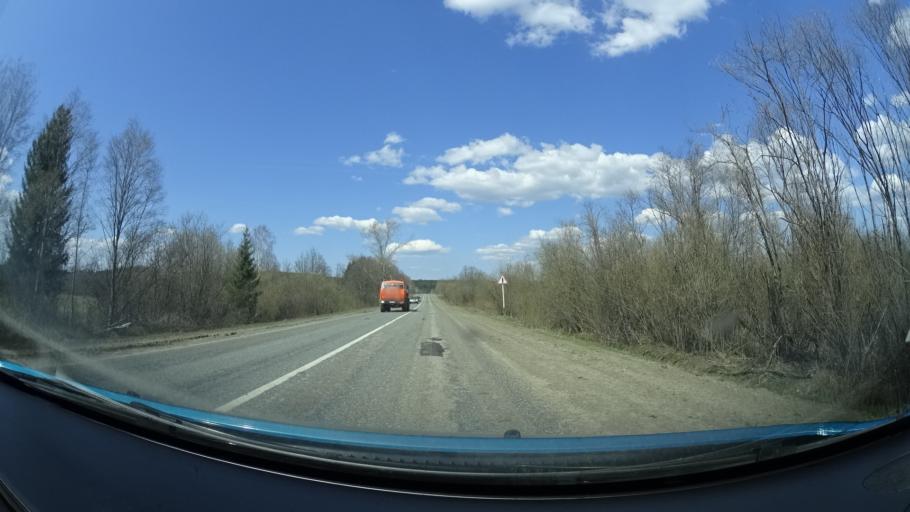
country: RU
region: Perm
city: Yugo-Kamskiy
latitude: 57.5353
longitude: 55.6895
